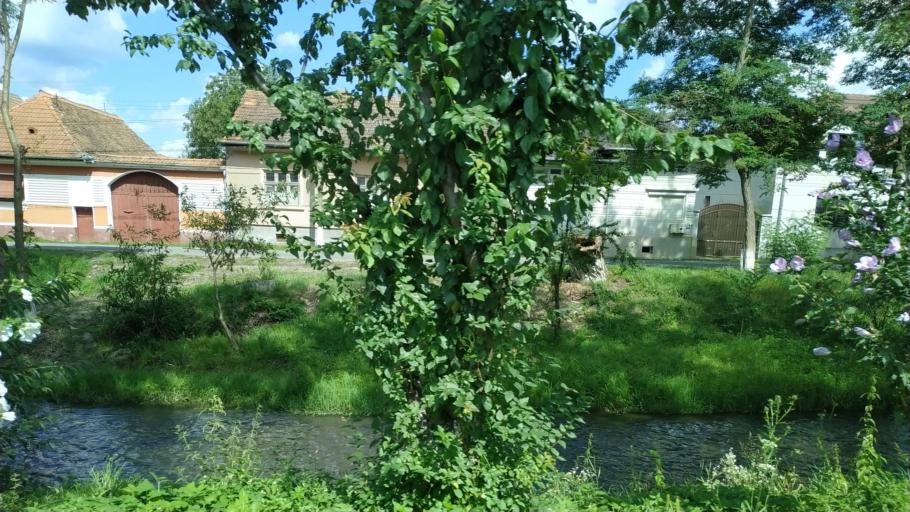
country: RO
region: Brasov
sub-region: Comuna Beclean
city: Beclean
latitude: 45.8309
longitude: 24.9238
